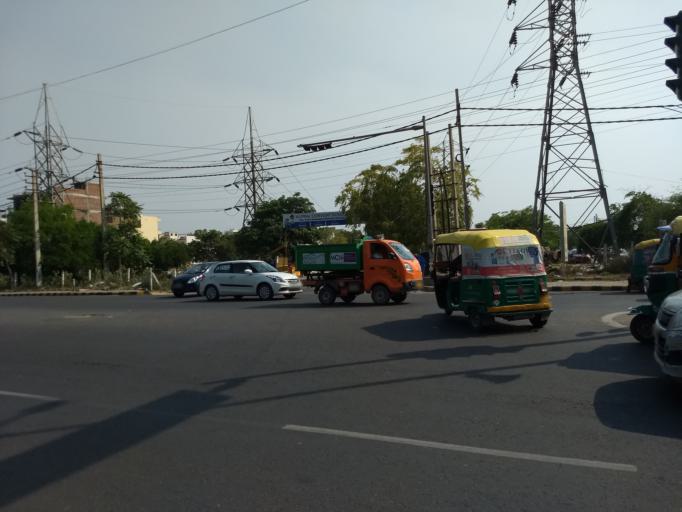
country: IN
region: Haryana
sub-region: Gurgaon
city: Gurgaon
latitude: 28.4394
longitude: 77.0429
